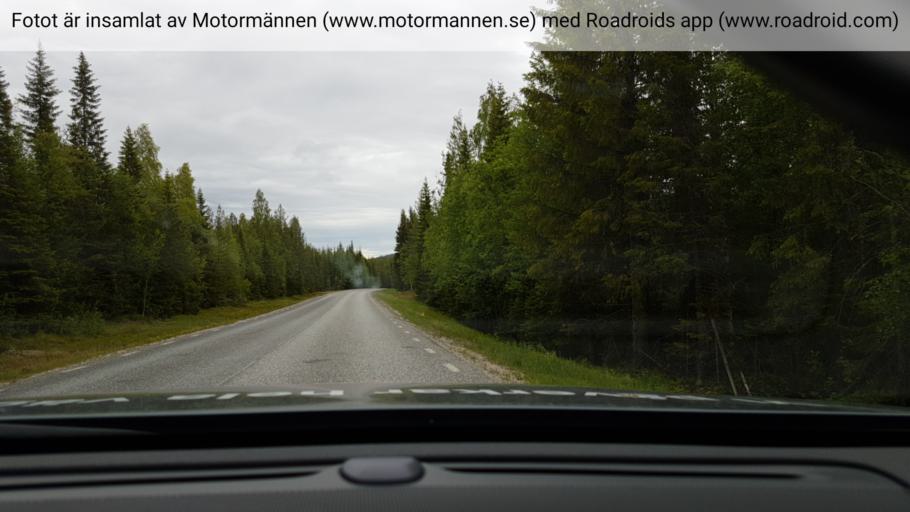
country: SE
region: Vaesterbotten
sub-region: Asele Kommun
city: Insjon
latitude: 64.3481
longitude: 17.8631
